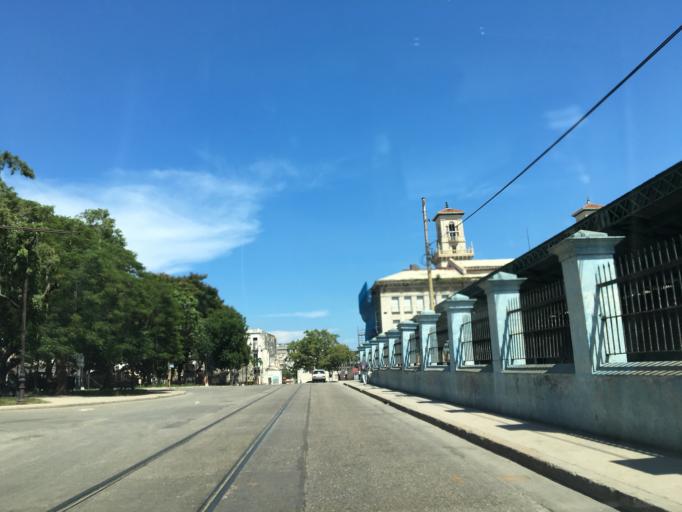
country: CU
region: La Habana
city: La Habana Vieja
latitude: 23.1299
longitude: -82.3558
